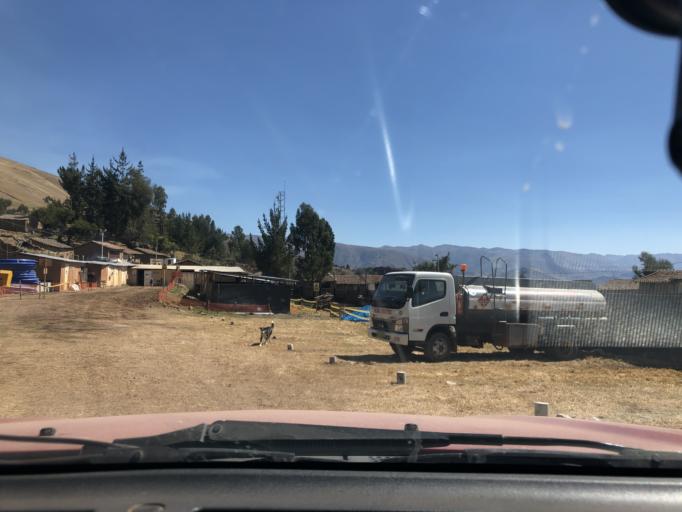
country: PE
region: Ayacucho
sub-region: Provincia de La Mar
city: Chilcas
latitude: -13.1684
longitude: -73.8485
